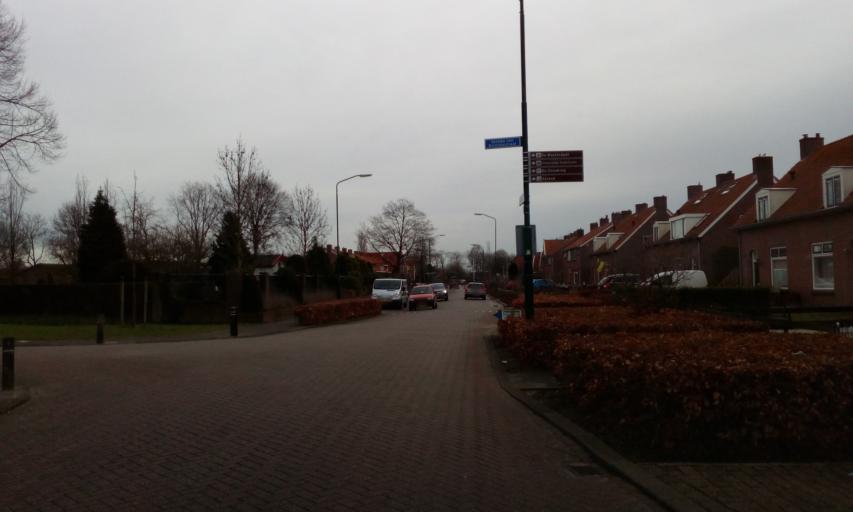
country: NL
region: North Brabant
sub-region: Gemeente Woudrichem
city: Woudrichem
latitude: 51.8140
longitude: 4.9980
